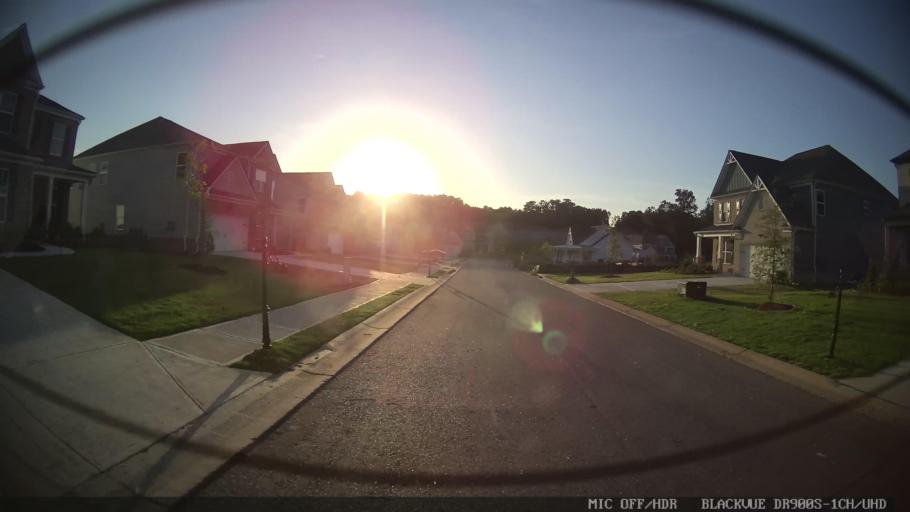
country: US
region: Georgia
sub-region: Forsyth County
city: Cumming
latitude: 34.2190
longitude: -84.2090
